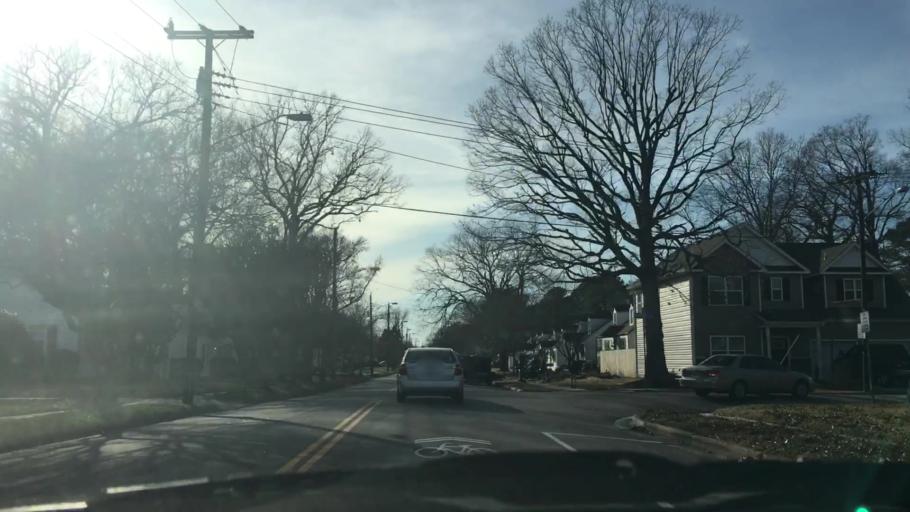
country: US
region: Virginia
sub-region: City of Norfolk
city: Norfolk
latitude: 36.8790
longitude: -76.2285
